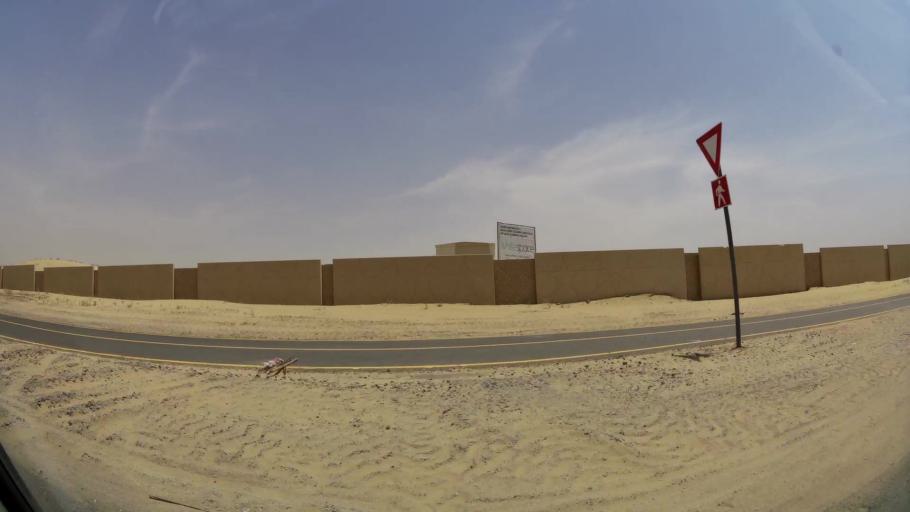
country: AE
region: Ash Shariqah
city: Sharjah
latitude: 25.2407
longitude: 55.4971
